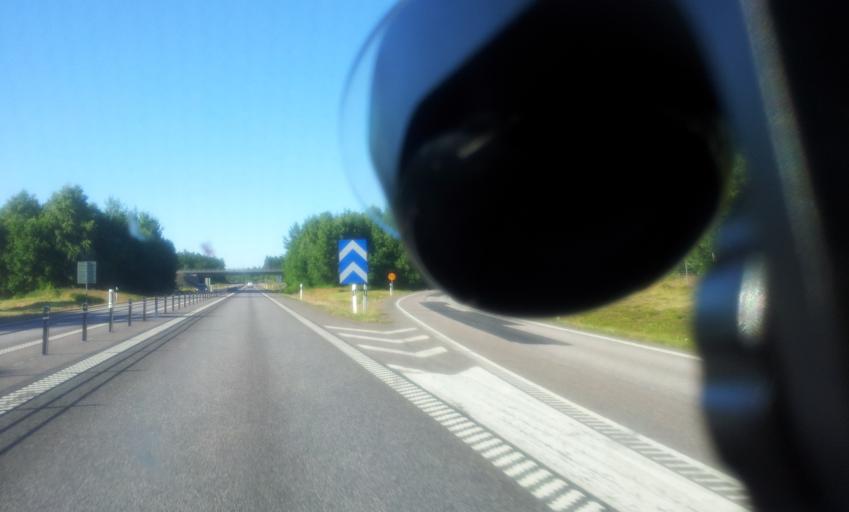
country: SE
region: Kalmar
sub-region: Kalmar Kommun
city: Ljungbyholm
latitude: 56.5543
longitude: 16.0862
